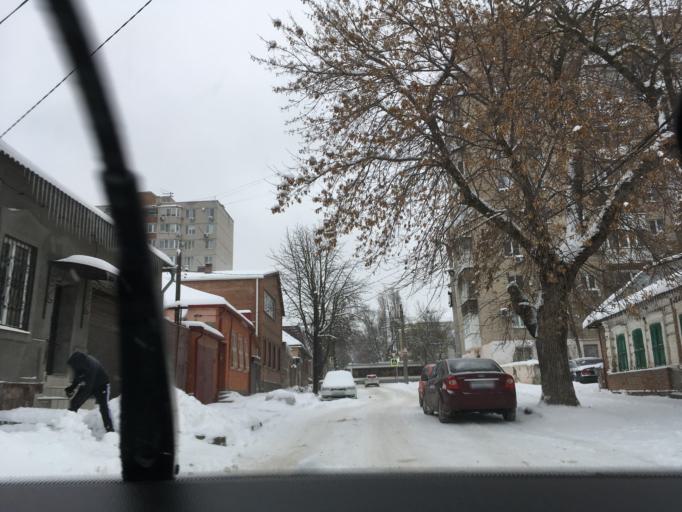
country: RU
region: Rostov
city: Rostov-na-Donu
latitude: 47.2266
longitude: 39.7556
